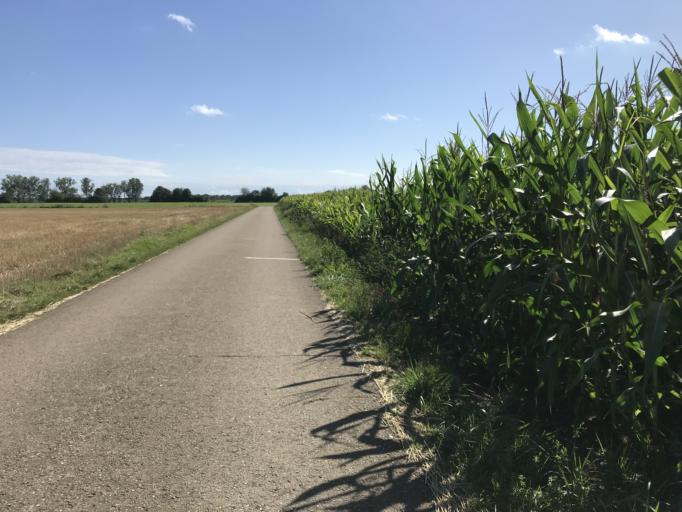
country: DE
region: Baden-Wuerttemberg
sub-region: Tuebingen Region
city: Langenau
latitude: 48.4759
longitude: 10.1214
